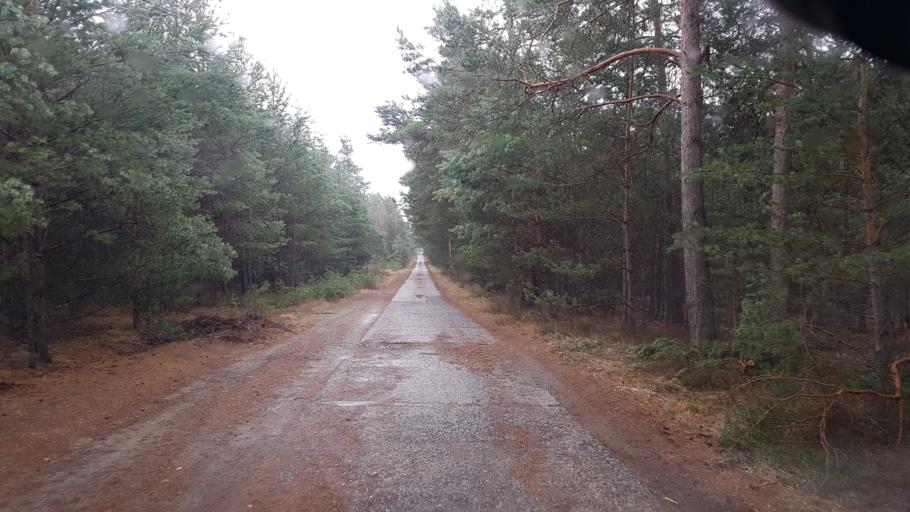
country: DE
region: Brandenburg
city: Grossraschen
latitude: 51.6078
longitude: 13.9874
